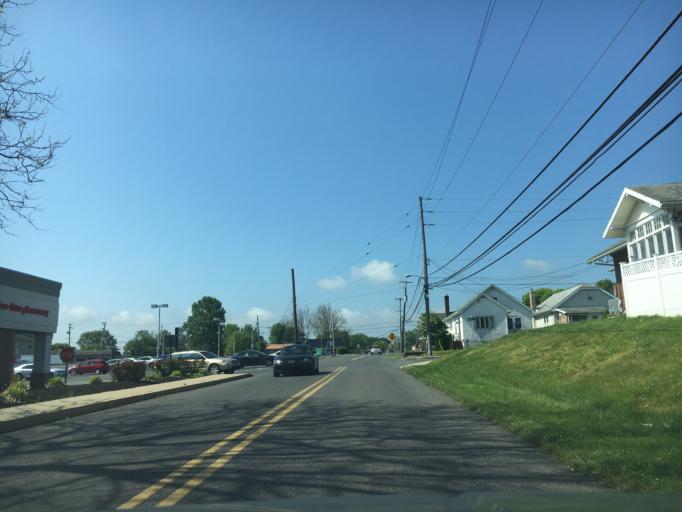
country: US
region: Pennsylvania
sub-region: Berks County
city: Boyertown
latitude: 40.3291
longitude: -75.6247
